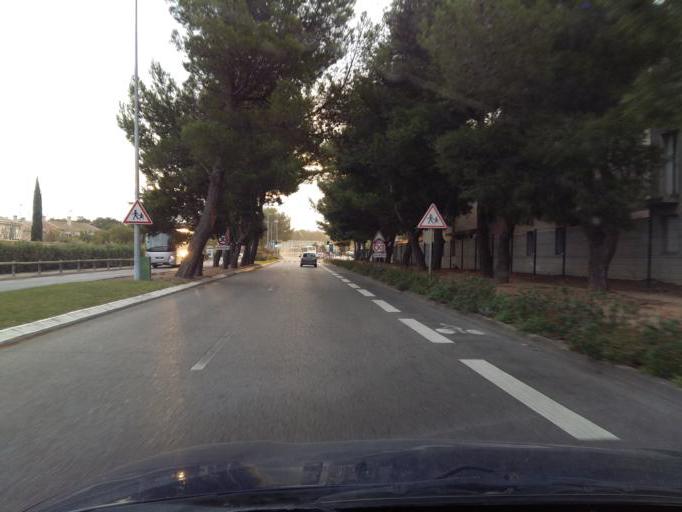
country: FR
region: Provence-Alpes-Cote d'Azur
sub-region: Departement des Bouches-du-Rhone
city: Istres
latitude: 43.4982
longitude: 4.9815
